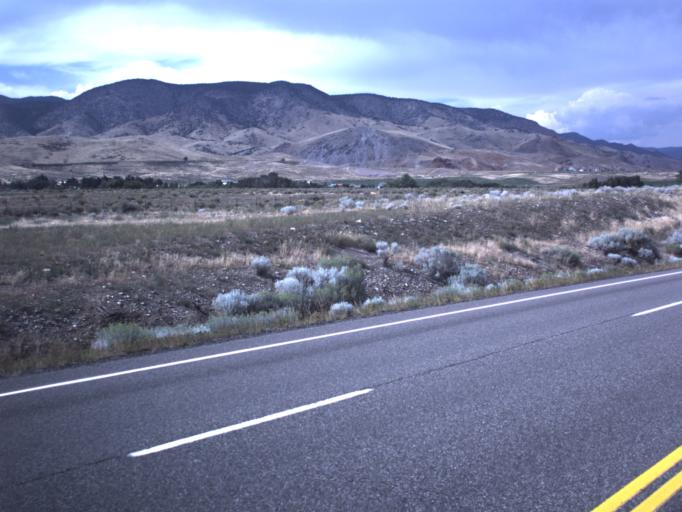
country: US
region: Utah
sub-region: Piute County
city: Junction
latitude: 38.4440
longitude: -112.2299
